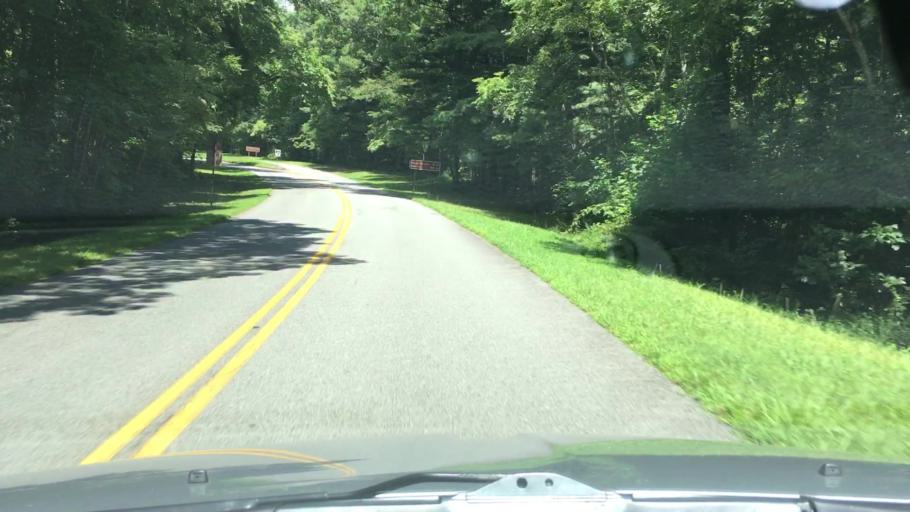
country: US
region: North Carolina
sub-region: Buncombe County
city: Asheville
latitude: 35.5913
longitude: -82.4785
